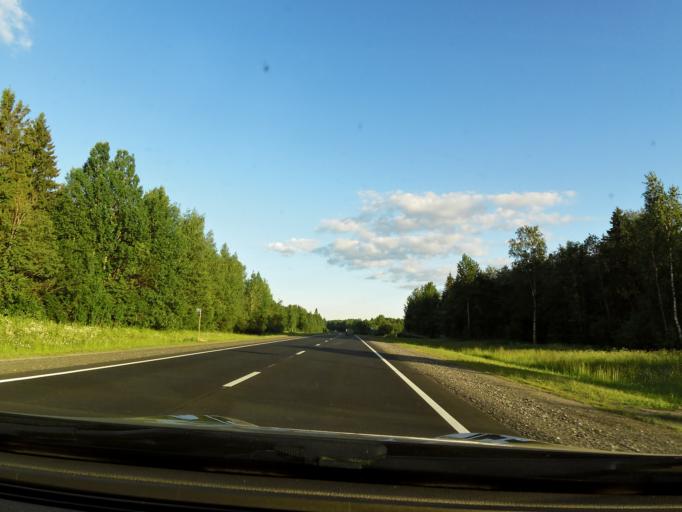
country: RU
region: Vologda
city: Gryazovets
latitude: 59.0119
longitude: 40.1204
